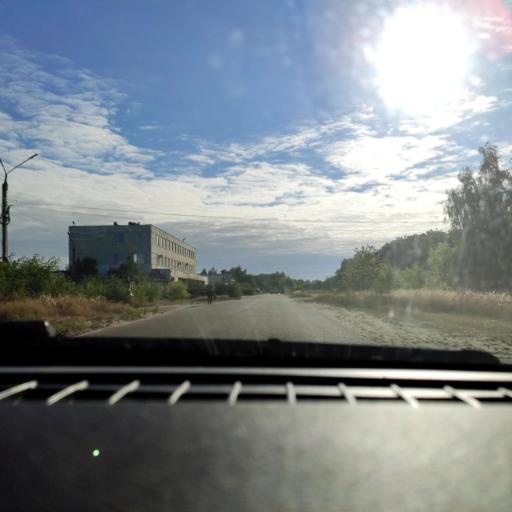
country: RU
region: Voronezj
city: Somovo
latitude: 51.7348
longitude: 39.3001
